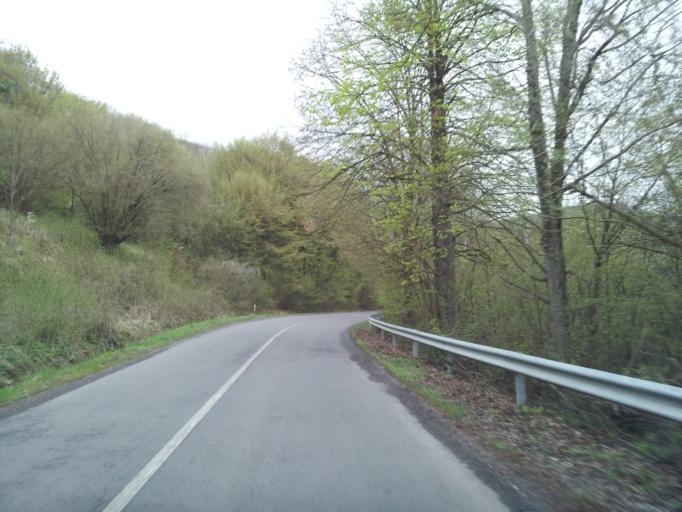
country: HU
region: Borsod-Abauj-Zemplen
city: Rudabanya
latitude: 48.4807
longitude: 20.5503
